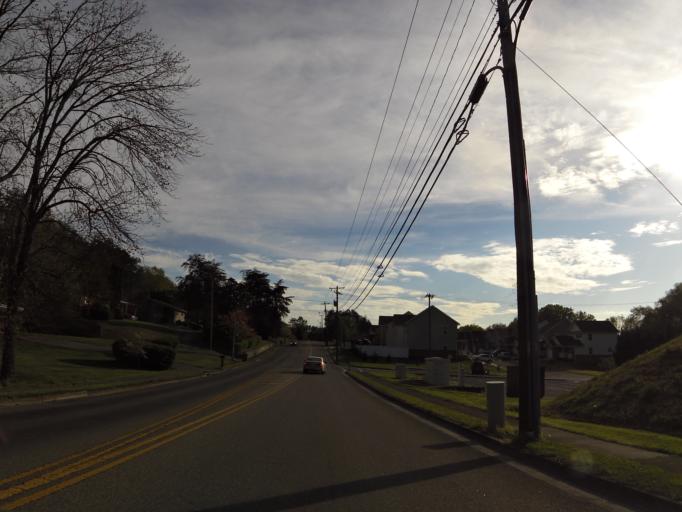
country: US
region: Tennessee
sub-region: Blount County
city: Maryville
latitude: 35.7400
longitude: -83.9723
